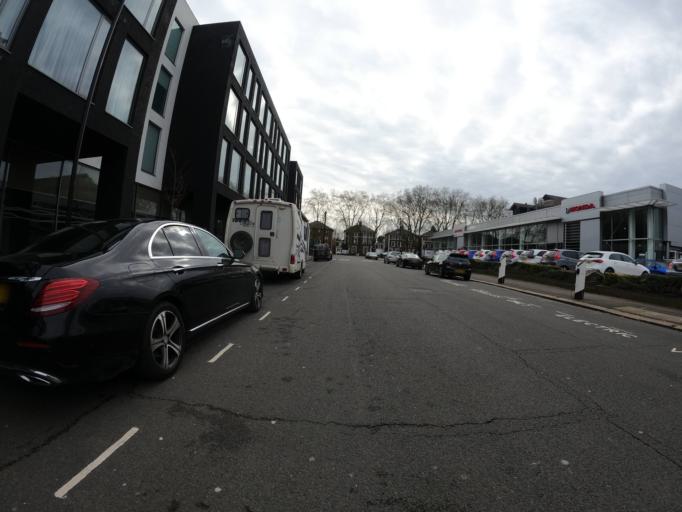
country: GB
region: England
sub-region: Greater London
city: Acton
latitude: 51.4930
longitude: -0.2791
